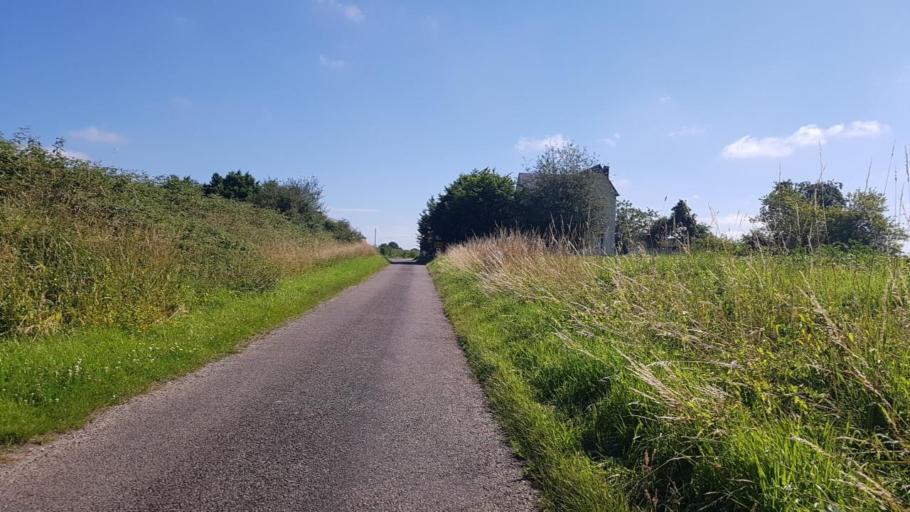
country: BE
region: Wallonia
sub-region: Province du Hainaut
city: Momignies
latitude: 50.0058
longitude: 4.1410
